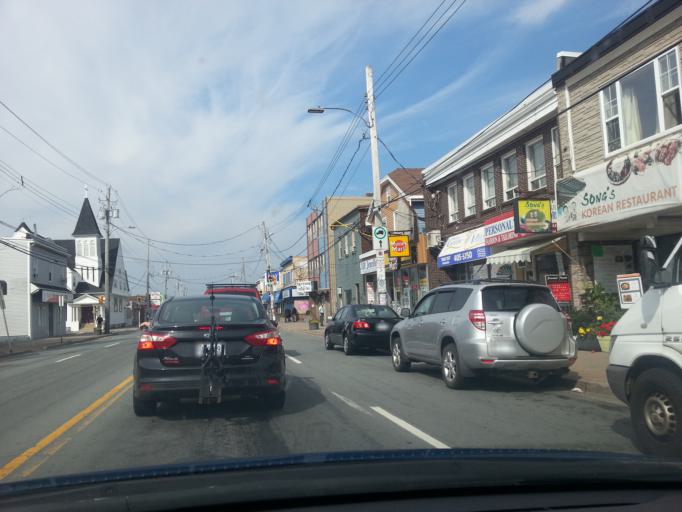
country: CA
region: Nova Scotia
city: Halifax
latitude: 44.6455
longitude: -63.5972
